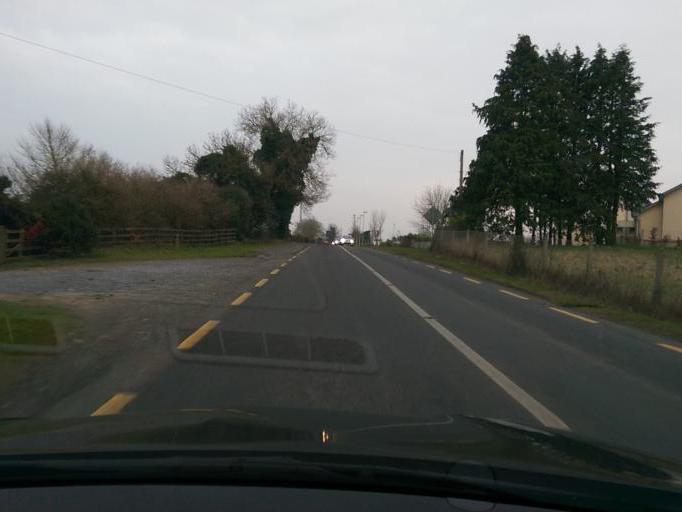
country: IE
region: Leinster
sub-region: An Longfort
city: Ballymahon
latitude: 53.5355
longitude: -7.7928
